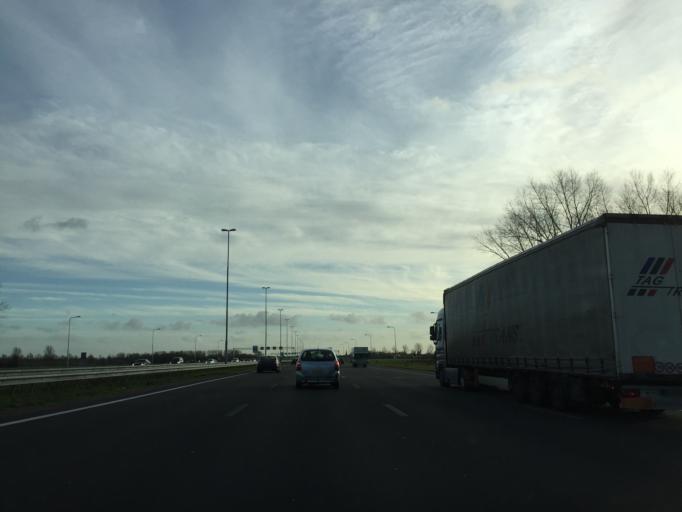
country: NL
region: Gelderland
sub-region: Gemeente Culemborg
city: Culemborg
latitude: 51.9109
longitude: 5.1804
